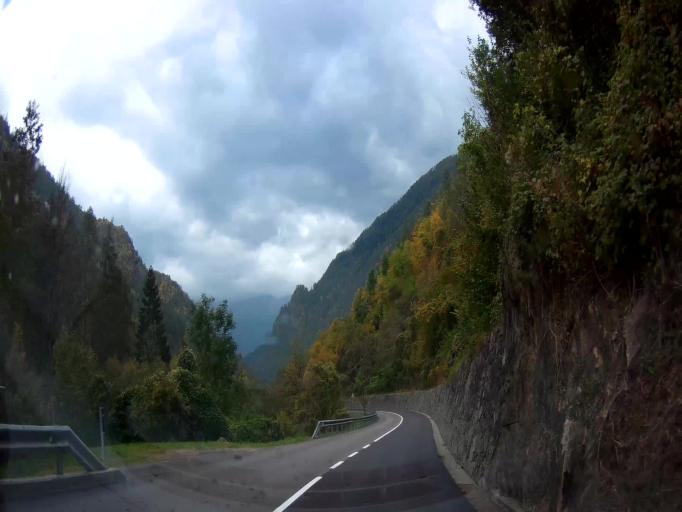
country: IT
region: Trentino-Alto Adige
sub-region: Bolzano
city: Certosa
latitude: 46.6835
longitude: 10.9343
